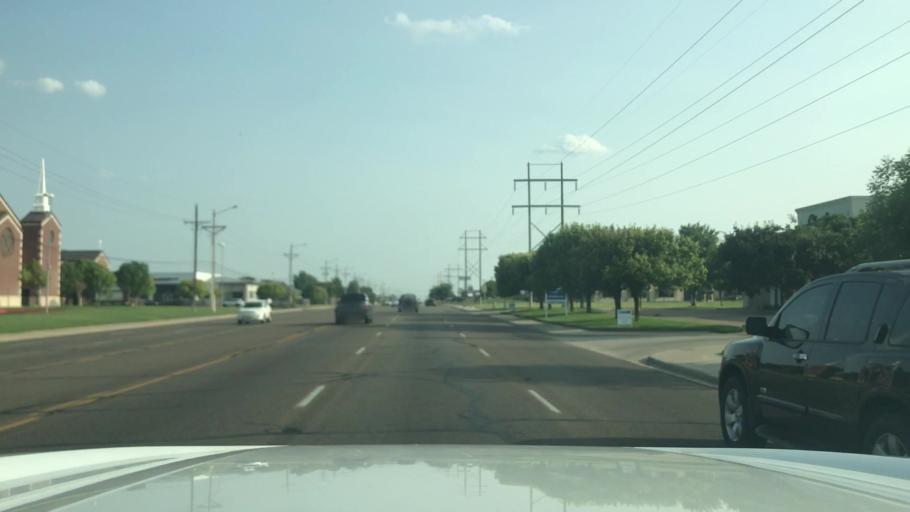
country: US
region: Texas
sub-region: Potter County
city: Amarillo
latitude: 35.1681
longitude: -101.9382
